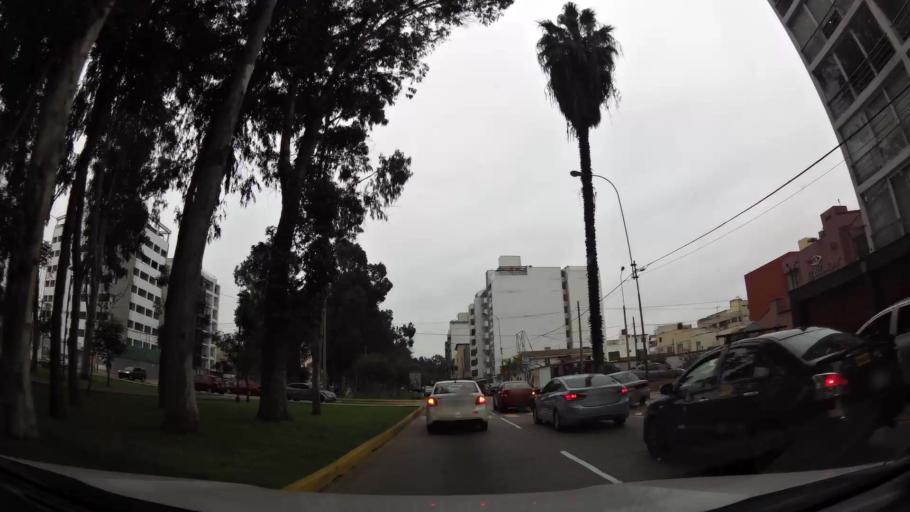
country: PE
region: Lima
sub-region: Lima
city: San Luis
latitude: -12.0940
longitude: -76.9994
